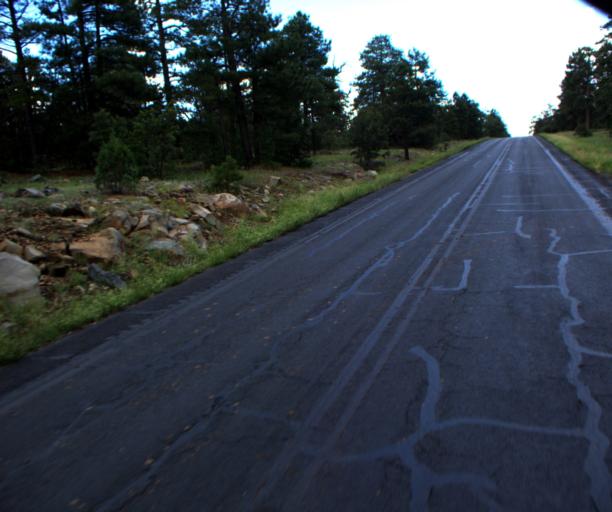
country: US
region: Arizona
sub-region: Gila County
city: Pine
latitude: 34.5065
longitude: -111.4725
